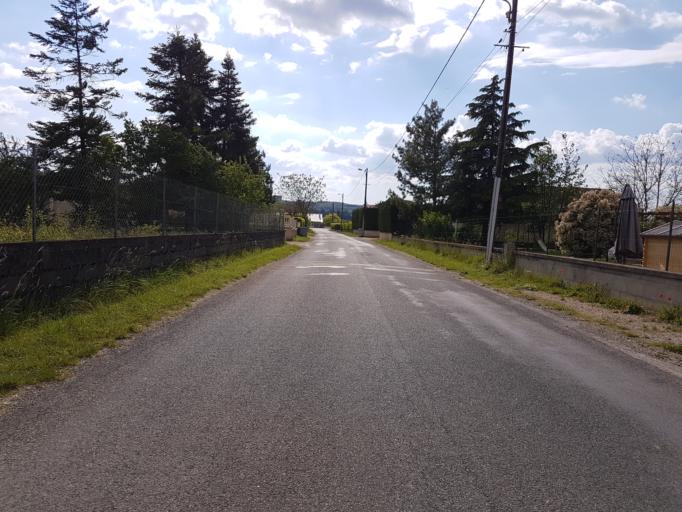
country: FR
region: Rhone-Alpes
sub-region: Departement de l'Isere
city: Bouvesse-Quirieu
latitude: 45.8088
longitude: 5.4436
